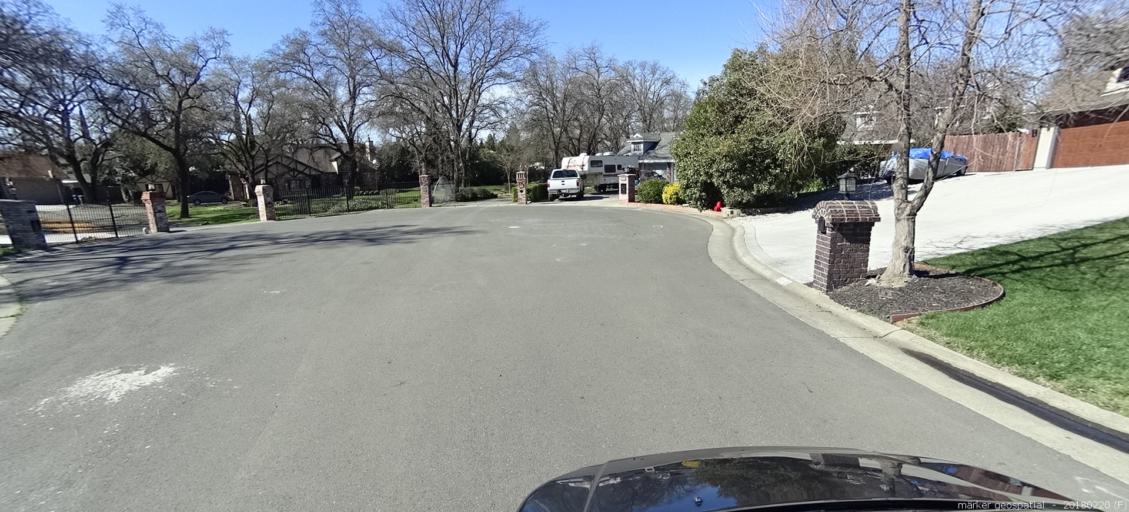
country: US
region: California
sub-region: Sacramento County
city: Orangevale
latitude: 38.6900
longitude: -121.2361
